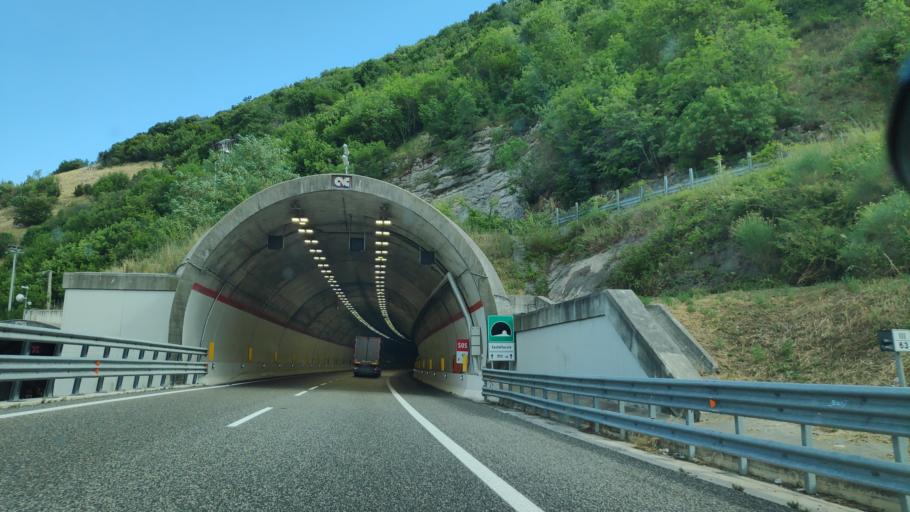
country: IT
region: Campania
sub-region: Provincia di Salerno
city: Sicignano degli Alburni
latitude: 40.5833
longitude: 15.3415
